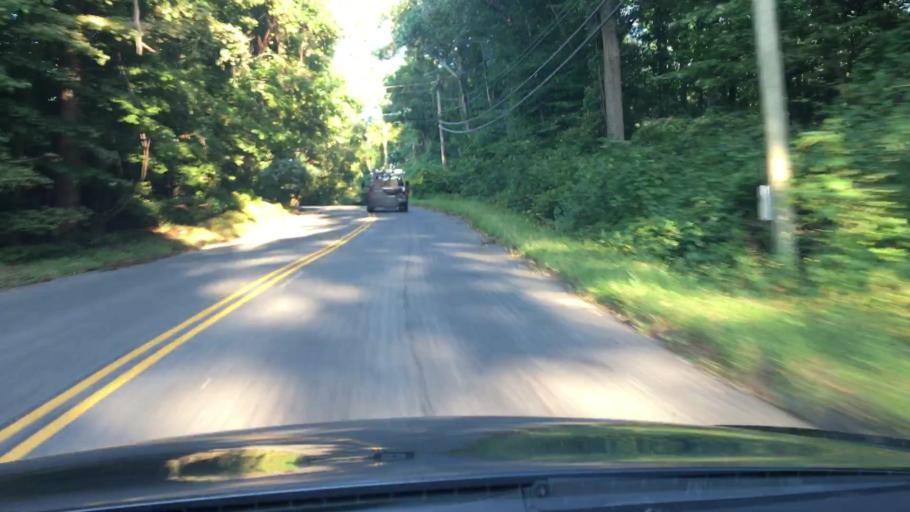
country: US
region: Connecticut
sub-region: Litchfield County
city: New Milford
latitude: 41.6092
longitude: -73.3876
